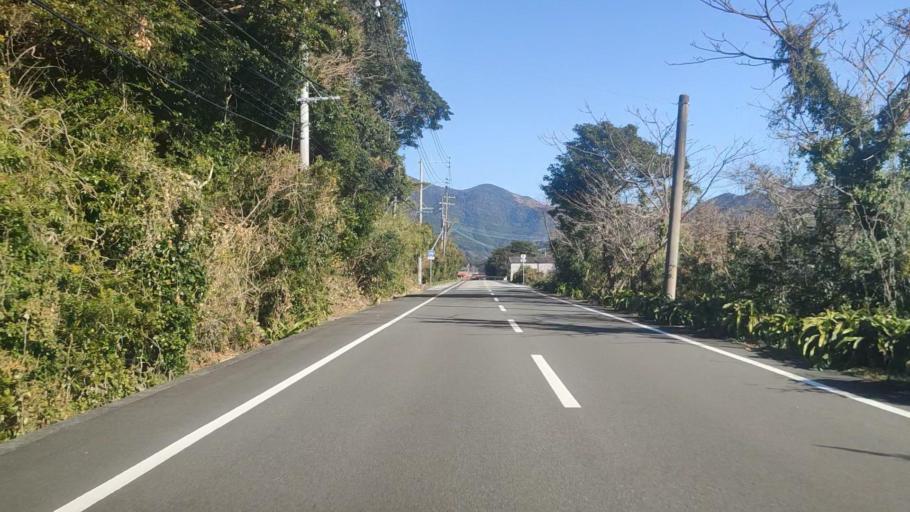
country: JP
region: Oita
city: Saiki
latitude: 32.7990
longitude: 131.8874
